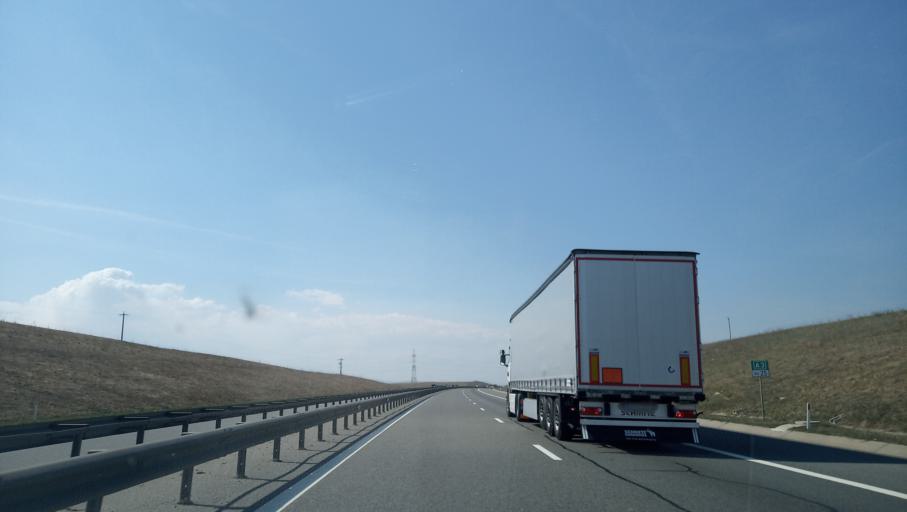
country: RO
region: Cluj
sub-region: Comuna Petrestii De Jos
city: Petrestii de Jos
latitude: 46.5975
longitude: 23.6411
